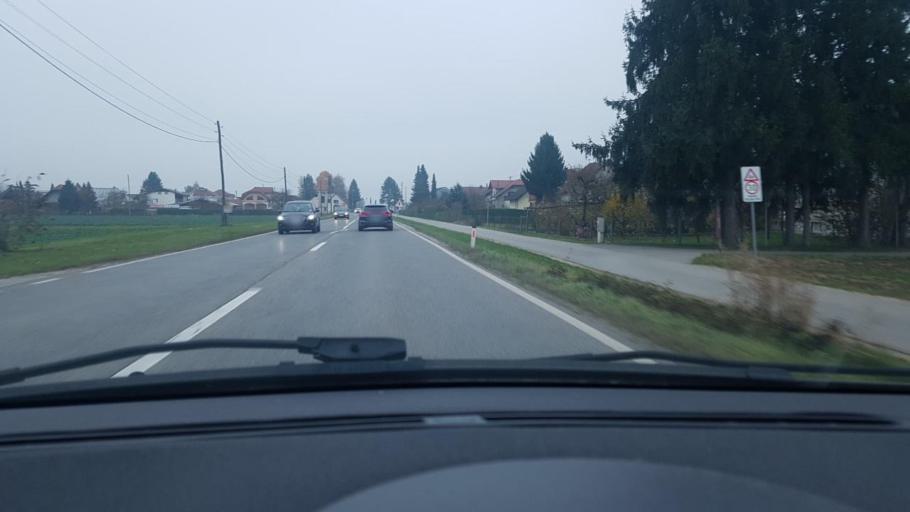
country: SI
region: Zalec
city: Zalec
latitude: 46.2454
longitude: 15.1985
